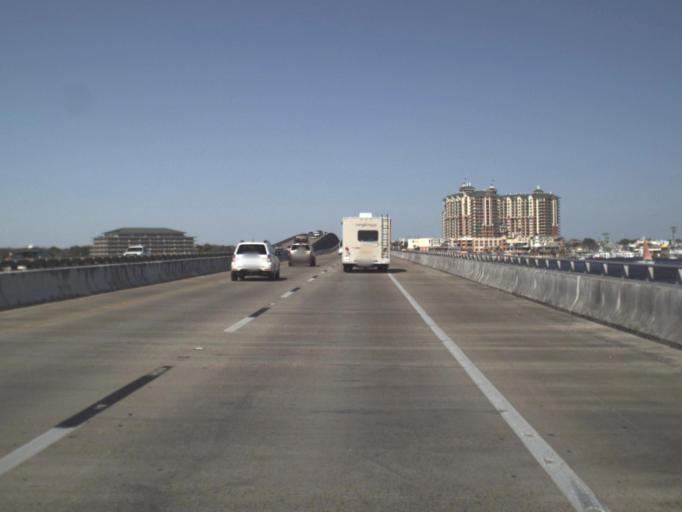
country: US
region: Florida
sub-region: Okaloosa County
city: Destin
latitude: 30.3918
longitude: -86.5215
